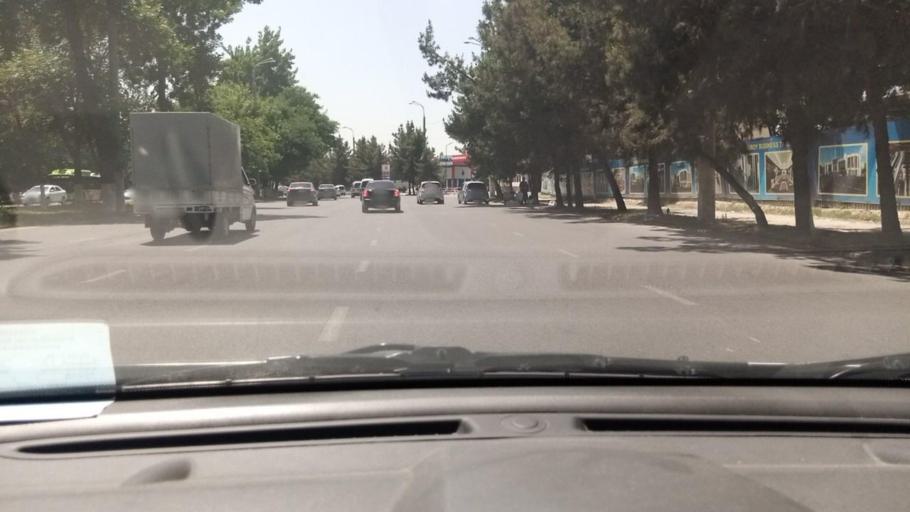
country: UZ
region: Toshkent Shahri
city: Tashkent
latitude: 41.2571
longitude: 69.2161
